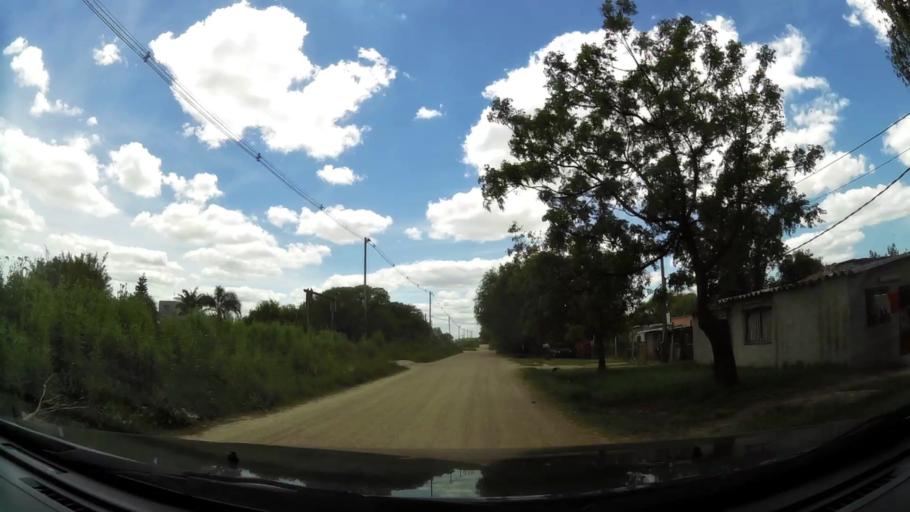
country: UY
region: Canelones
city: Colonia Nicolich
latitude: -34.8179
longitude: -56.0012
